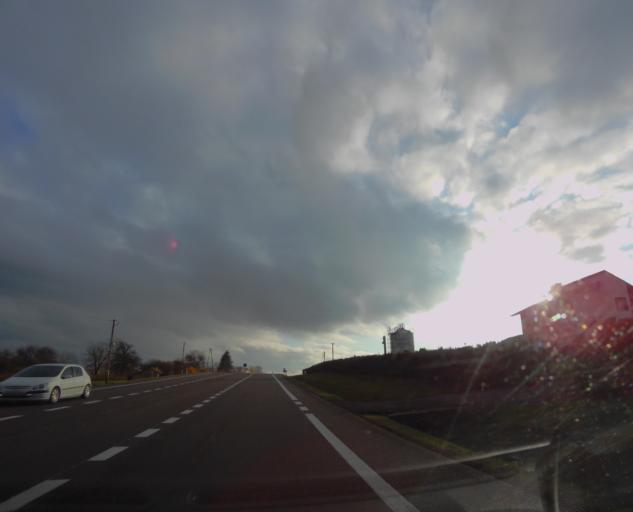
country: PL
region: Subcarpathian Voivodeship
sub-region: Powiat przemyski
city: Orly
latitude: 49.8914
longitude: 22.8164
